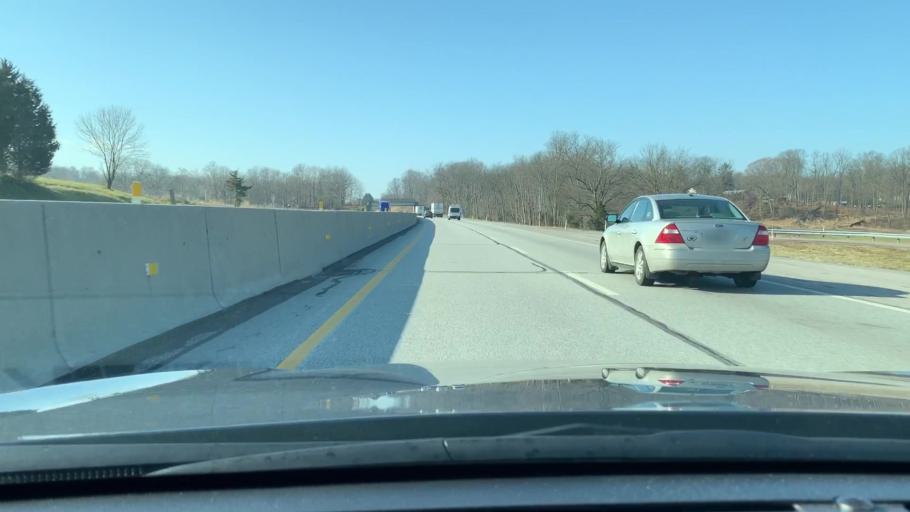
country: US
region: Pennsylvania
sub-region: Lancaster County
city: Elizabethtown
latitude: 40.2091
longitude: -76.6148
